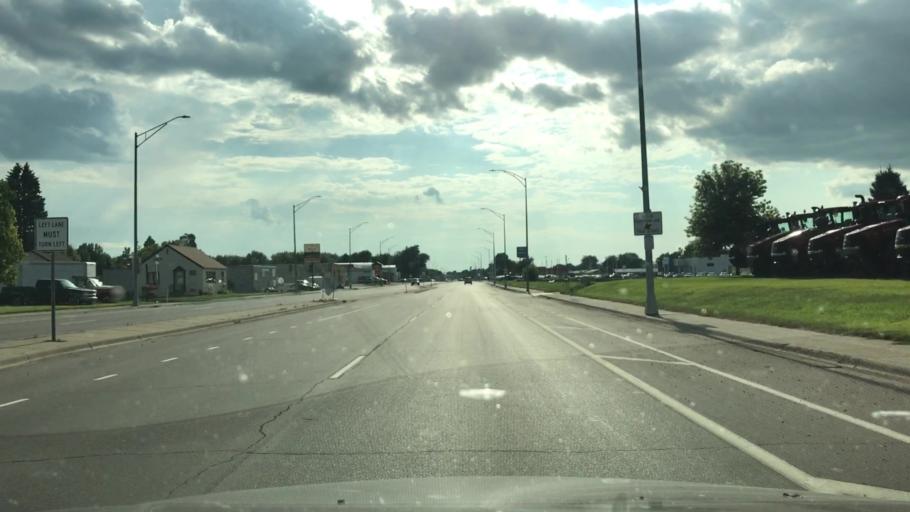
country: US
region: Minnesota
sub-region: Nobles County
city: Worthington
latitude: 43.6311
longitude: -95.5828
